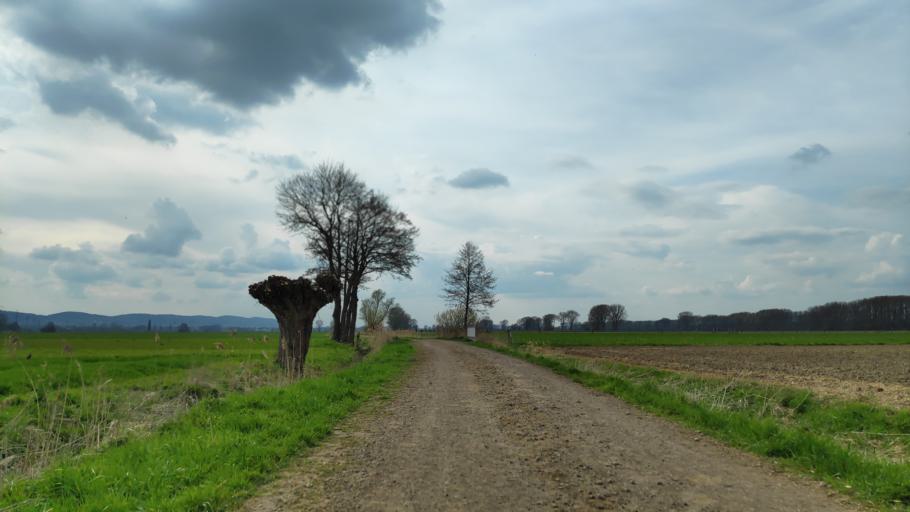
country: DE
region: North Rhine-Westphalia
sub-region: Regierungsbezirk Detmold
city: Minden
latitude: 52.2869
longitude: 8.8613
